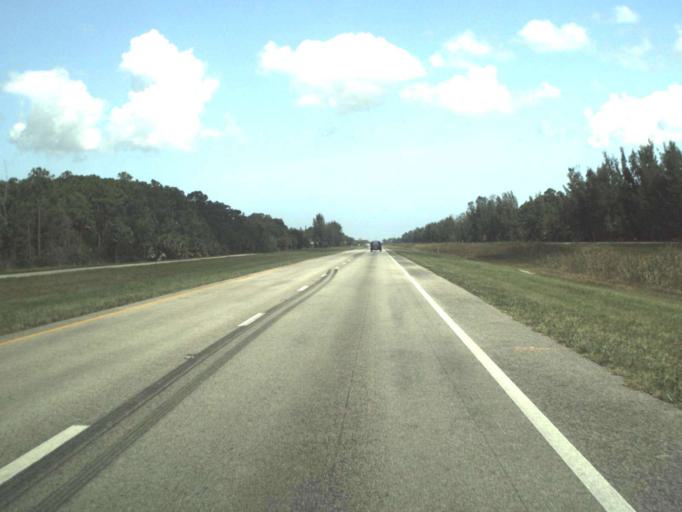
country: US
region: Florida
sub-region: Palm Beach County
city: Palm Beach Gardens
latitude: 26.8351
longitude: -80.1902
